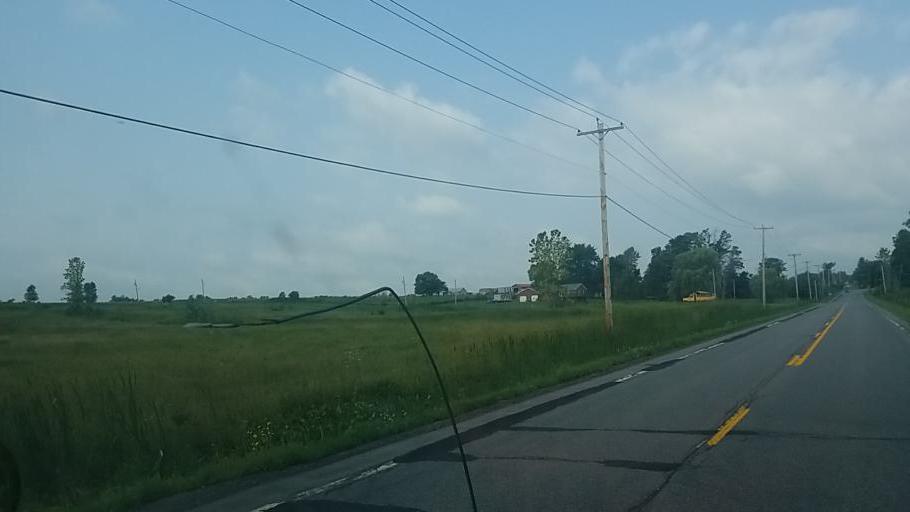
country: US
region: New York
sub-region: Fulton County
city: Johnstown
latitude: 43.0190
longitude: -74.4000
